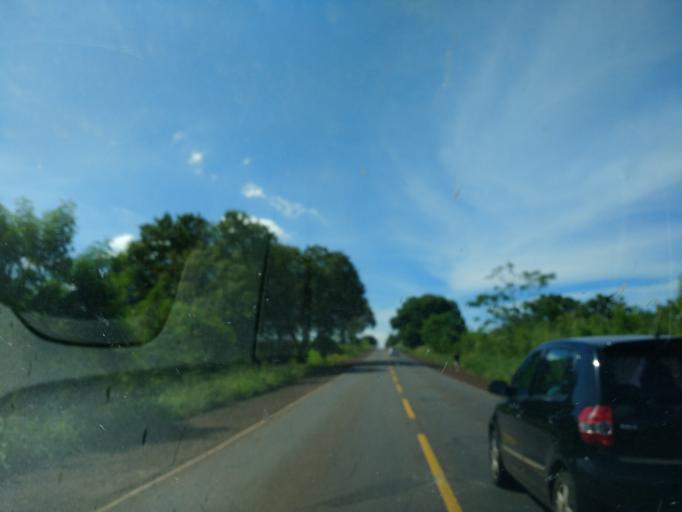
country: BR
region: Parana
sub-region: Paicandu
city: Paicandu
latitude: -23.5586
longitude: -52.2438
